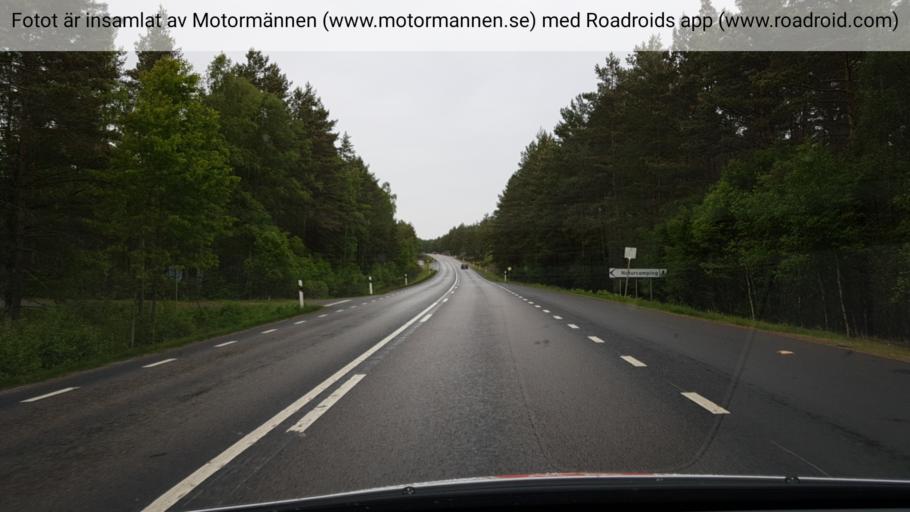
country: SE
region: Kalmar
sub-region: Hultsfreds Kommun
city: Malilla
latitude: 57.3949
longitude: 15.8076
